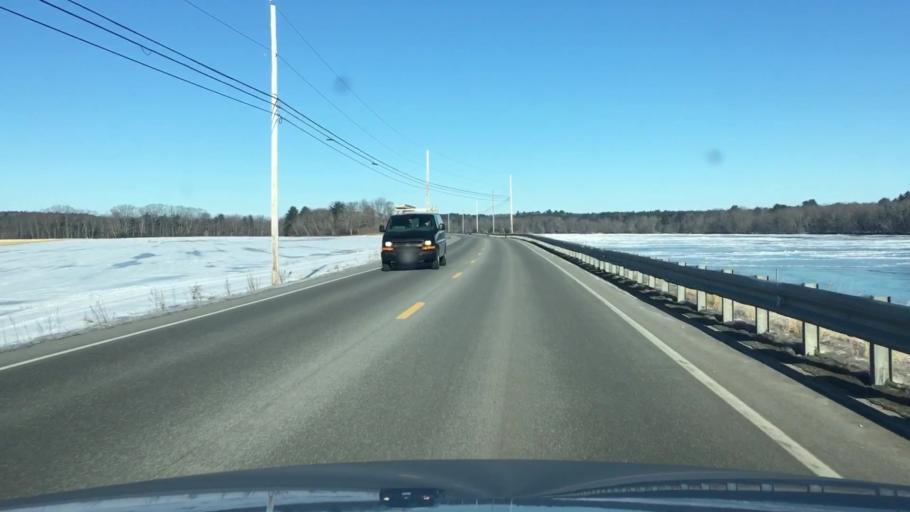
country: US
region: Maine
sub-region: Androscoggin County
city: Lisbon
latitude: 43.9889
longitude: -70.1378
